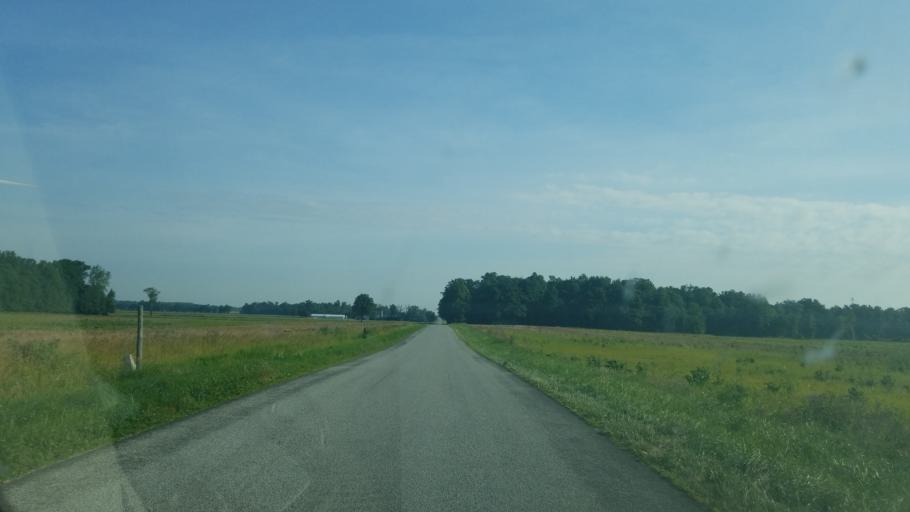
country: US
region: Ohio
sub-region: Hancock County
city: Arlington
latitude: 40.7919
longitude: -83.6708
